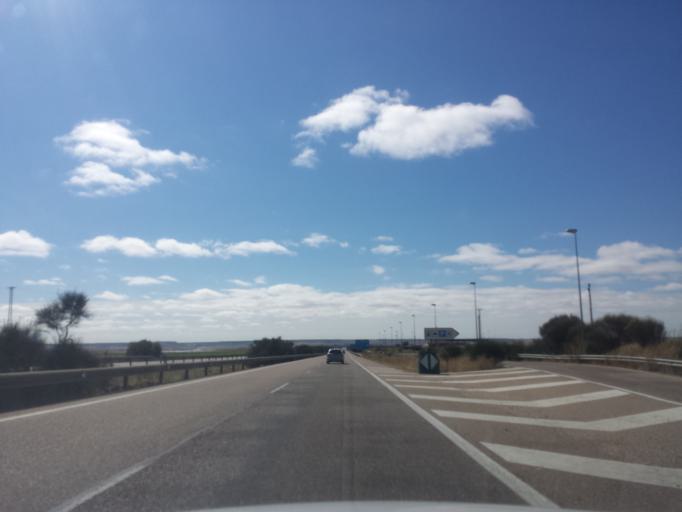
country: ES
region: Castille and Leon
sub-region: Provincia de Valladolid
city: San Pedro de Latarce
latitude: 41.7770
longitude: -5.3145
